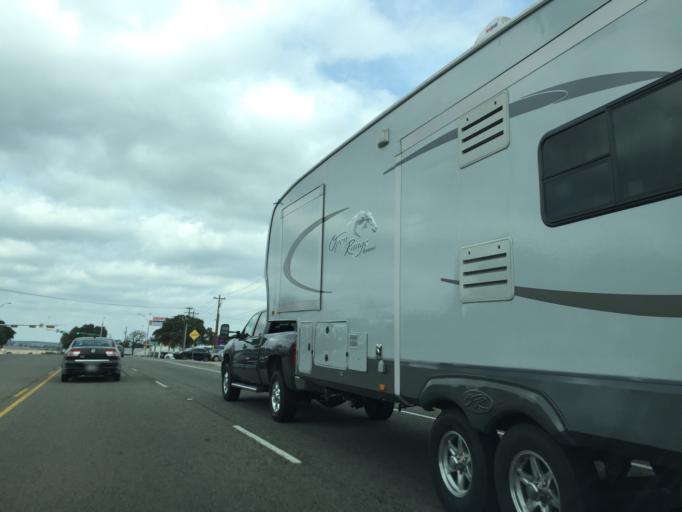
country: US
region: Texas
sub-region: Travis County
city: Briarcliff
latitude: 30.4605
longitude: -98.1578
